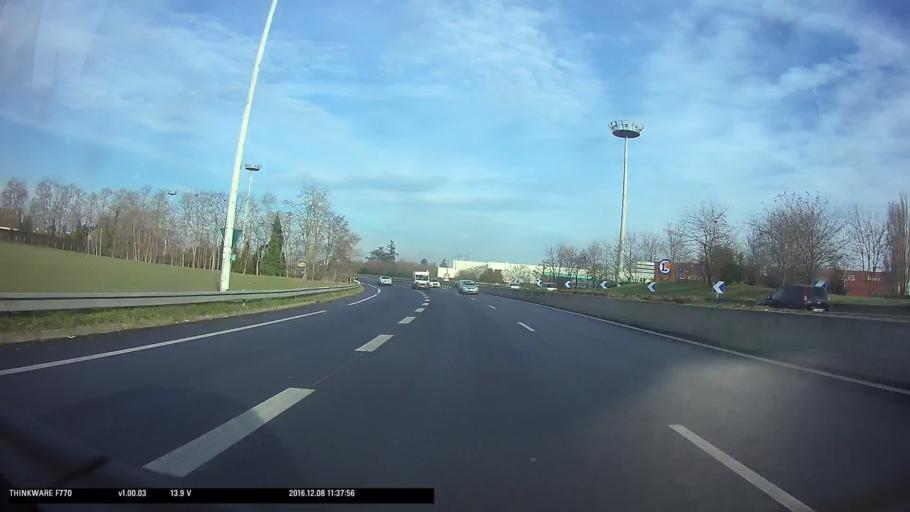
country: FR
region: Ile-de-France
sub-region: Departement du Val-d'Oise
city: Pontoise
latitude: 49.0638
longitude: 2.0867
